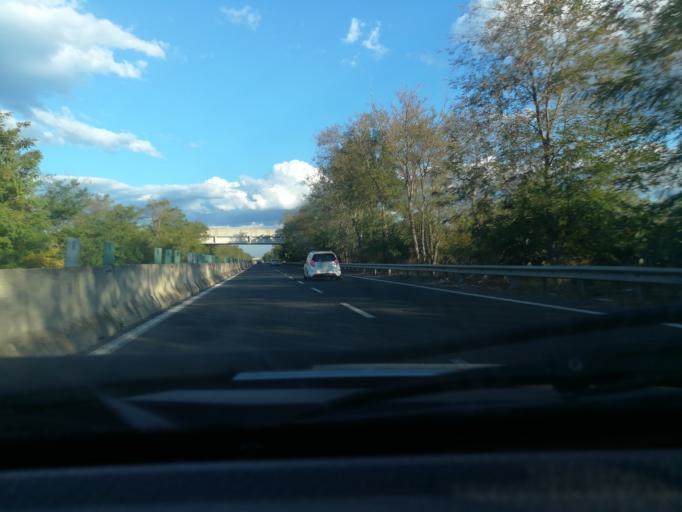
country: IT
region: Apulia
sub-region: Provincia di Bari
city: Mola di Bari
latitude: 41.0414
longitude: 17.1152
